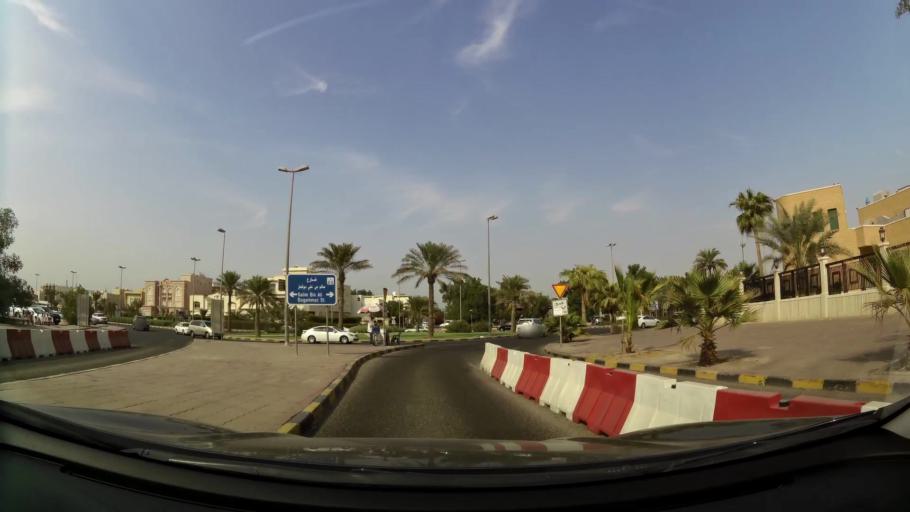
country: KW
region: Al Asimah
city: Ash Shamiyah
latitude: 29.3260
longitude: 47.9703
